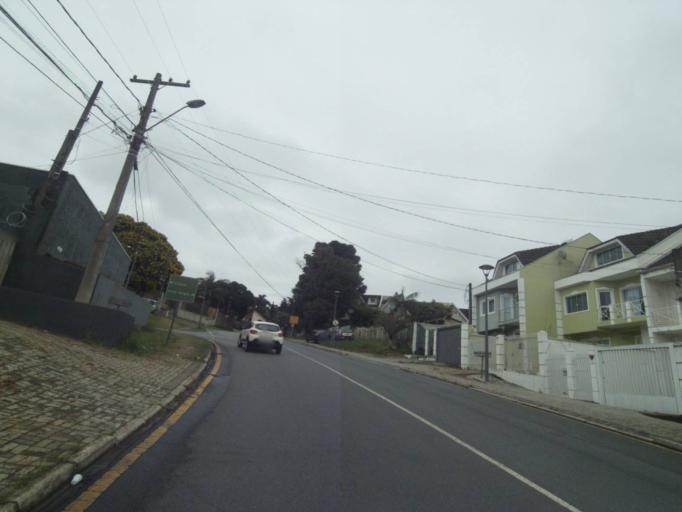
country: BR
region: Parana
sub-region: Curitiba
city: Curitiba
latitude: -25.4133
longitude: -49.2869
